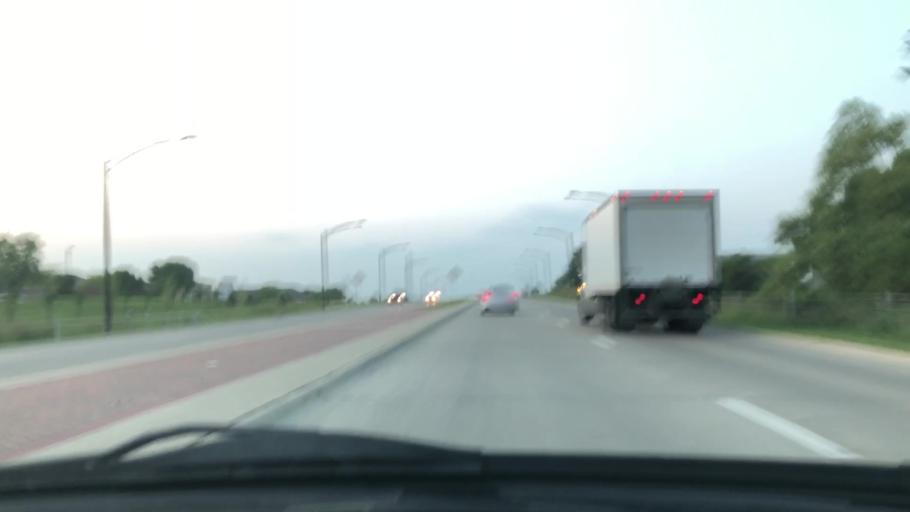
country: US
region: Iowa
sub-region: Johnson County
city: Coralville
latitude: 41.7045
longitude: -91.6081
